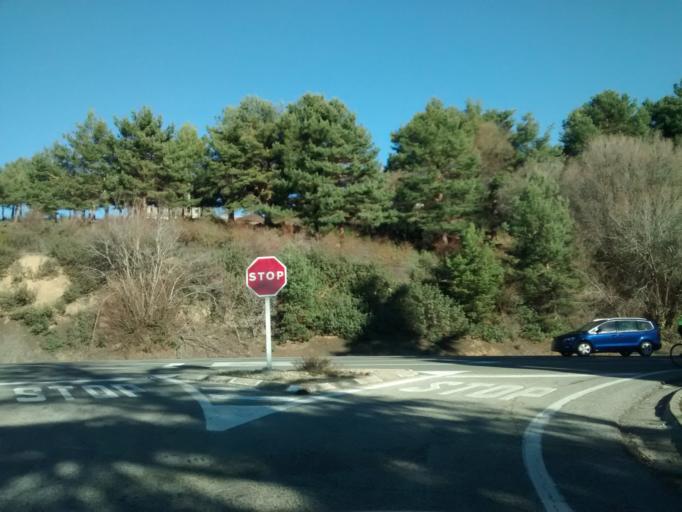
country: ES
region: Madrid
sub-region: Provincia de Madrid
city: Navacerrada
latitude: 40.7343
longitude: -4.0201
